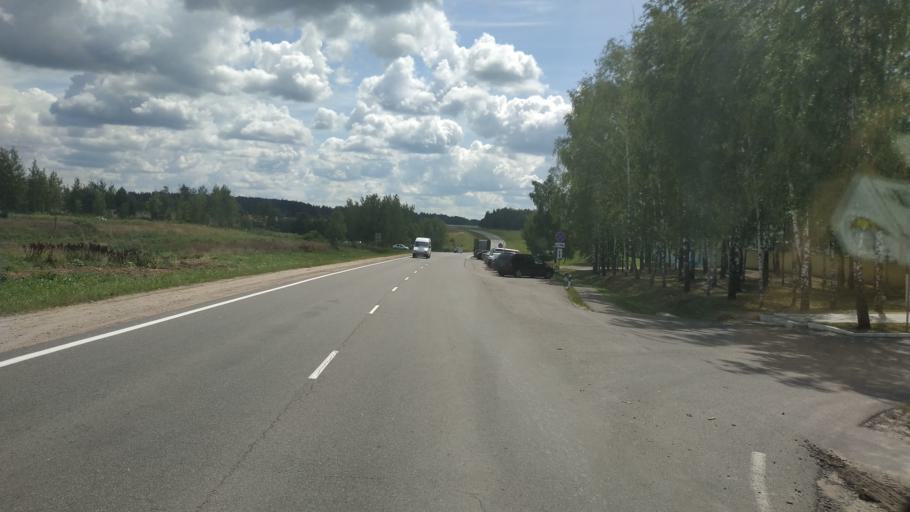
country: BY
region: Mogilev
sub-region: Mahilyowski Rayon
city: Veyno
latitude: 53.8382
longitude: 30.3977
